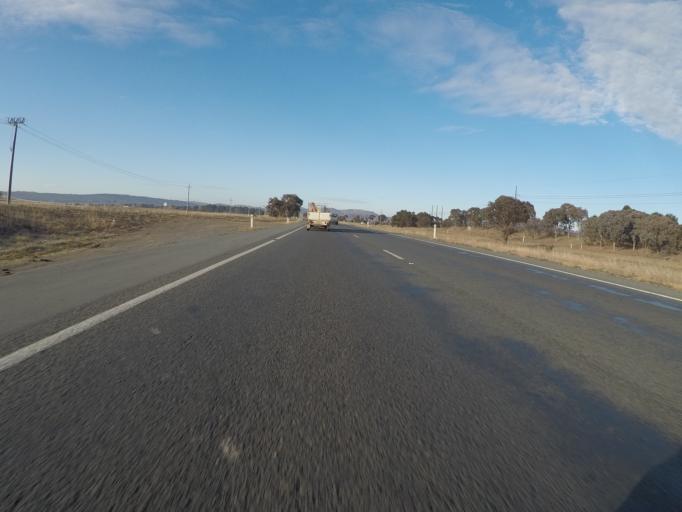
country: AU
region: Australian Capital Territory
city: Forrest
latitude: -35.3477
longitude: 149.1637
